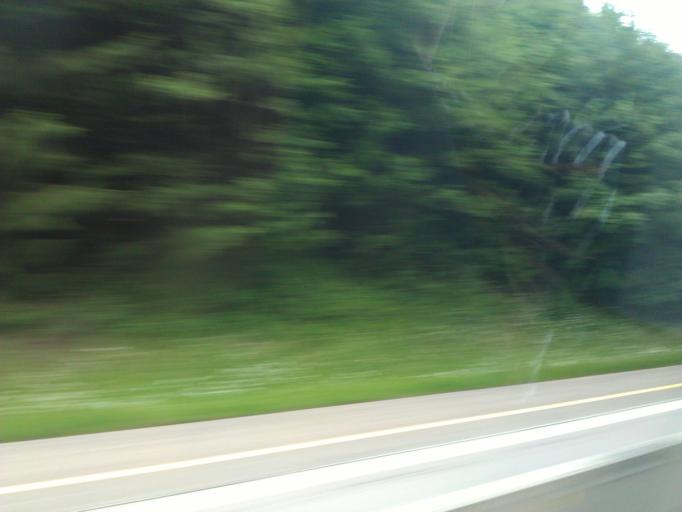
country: DE
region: Rheinland-Pfalz
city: Hinzert-Polert
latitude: 49.7166
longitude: 6.8936
